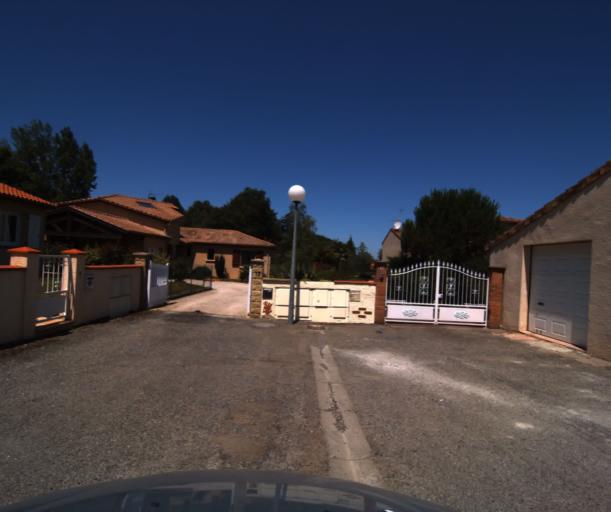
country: FR
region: Midi-Pyrenees
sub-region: Departement de la Haute-Garonne
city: Muret
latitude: 43.4588
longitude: 1.3419
